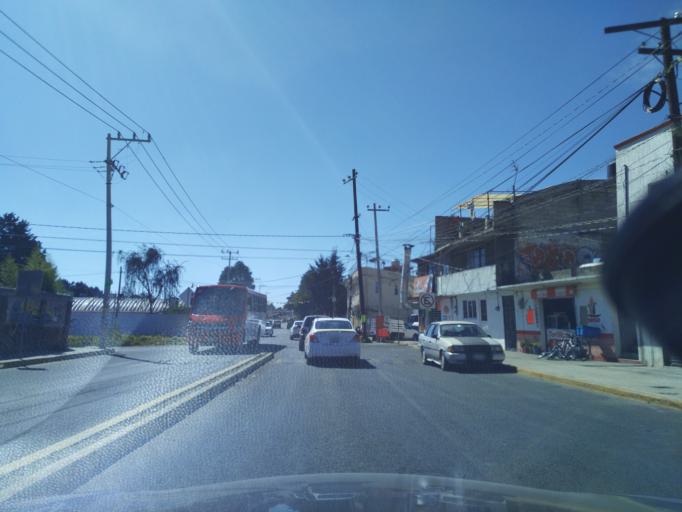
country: MX
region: Mexico
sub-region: Ocoyoacac
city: El Llano del Compromiso
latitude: 19.2551
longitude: -99.4724
